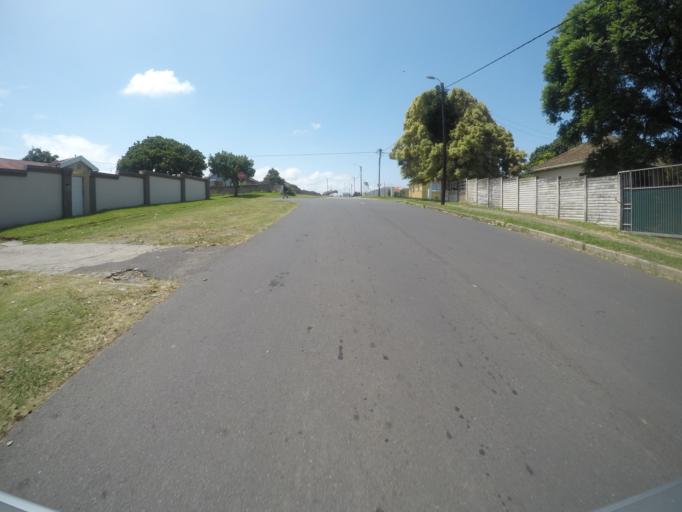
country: ZA
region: Eastern Cape
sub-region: Buffalo City Metropolitan Municipality
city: East London
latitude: -32.9728
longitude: 27.8711
